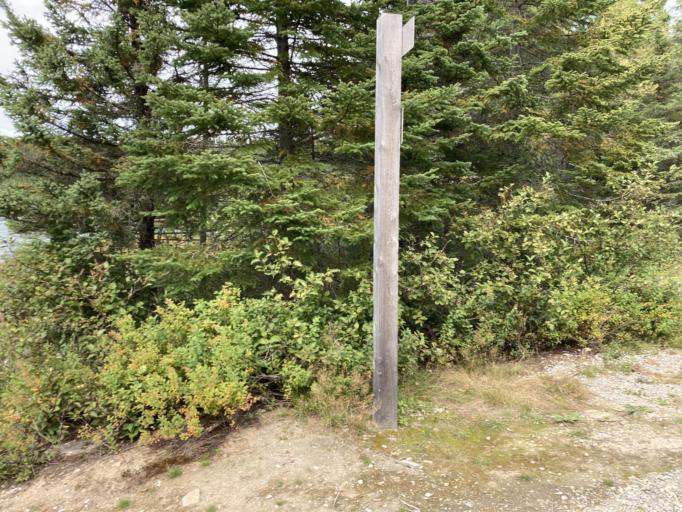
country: CA
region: Quebec
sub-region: Capitale-Nationale
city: Baie-Saint-Paul
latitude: 47.7188
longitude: -70.9195
